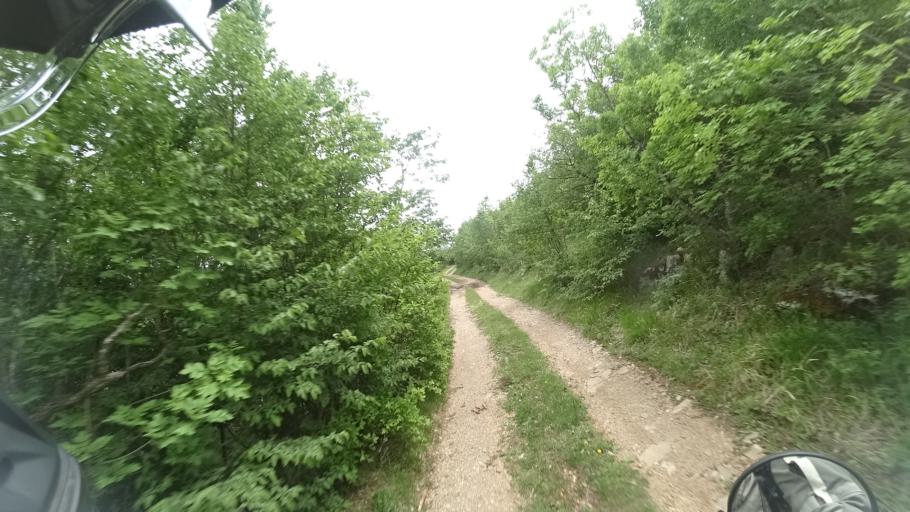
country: HR
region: Splitsko-Dalmatinska
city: Hrvace
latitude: 43.8930
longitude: 16.5507
